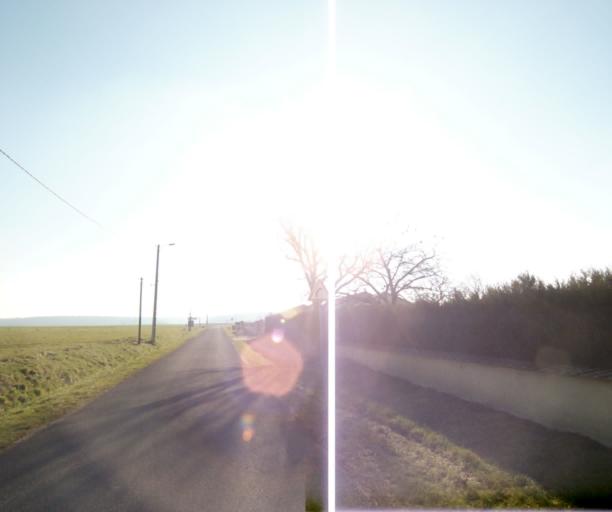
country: FR
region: Champagne-Ardenne
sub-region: Departement de la Haute-Marne
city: Bienville
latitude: 48.5406
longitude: 5.0186
